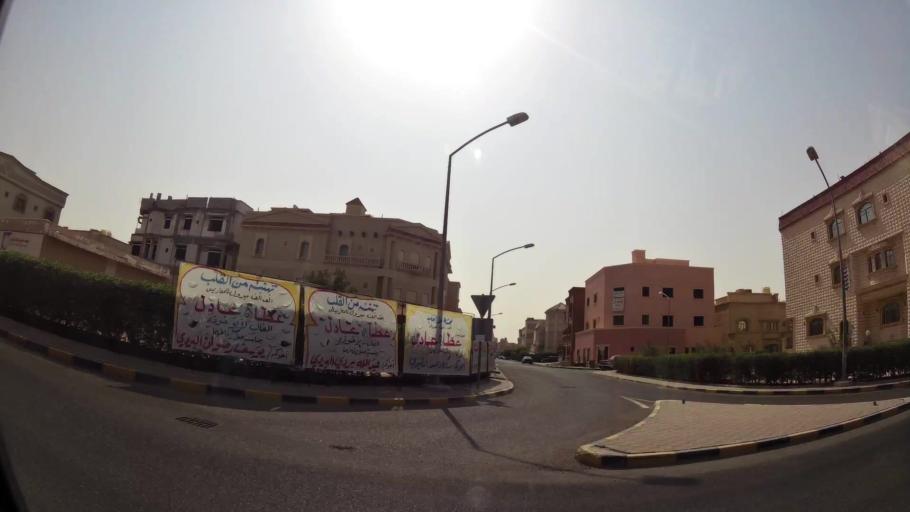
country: KW
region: Muhafazat al Jahra'
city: Al Jahra'
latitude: 29.3068
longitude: 47.7094
